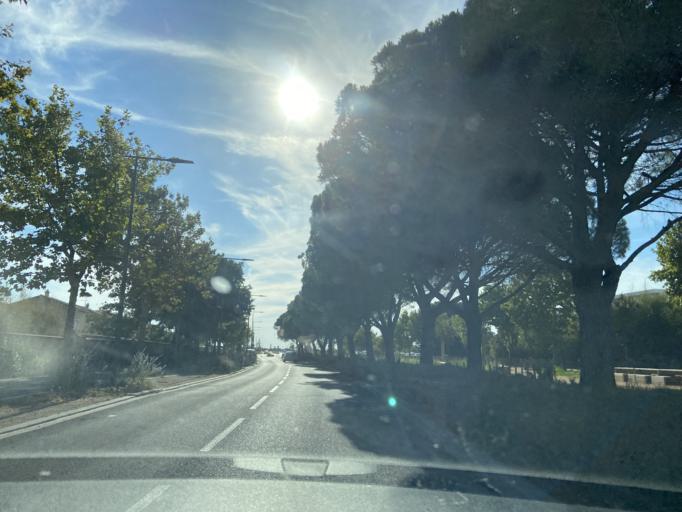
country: FR
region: Provence-Alpes-Cote d'Azur
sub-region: Departement des Bouches-du-Rhone
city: Miramas
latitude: 43.5883
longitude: 4.9966
